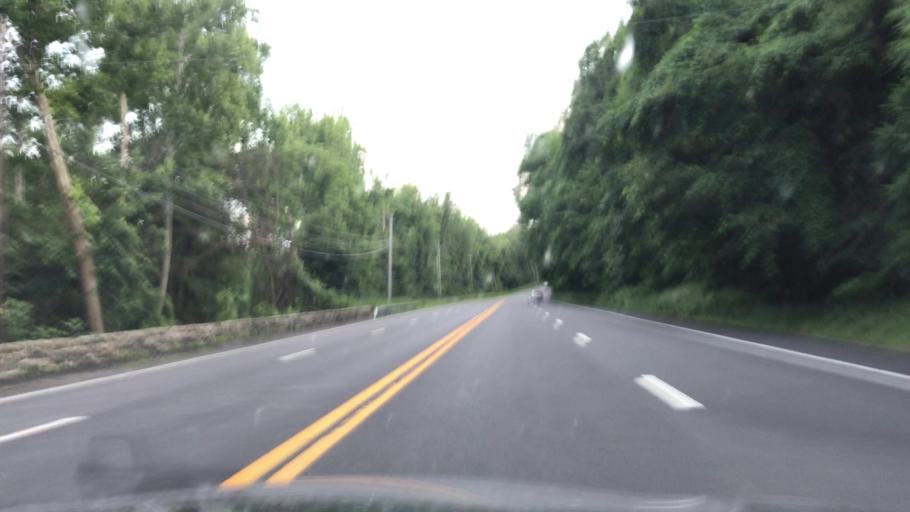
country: US
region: New York
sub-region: Orange County
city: Harriman
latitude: 41.2725
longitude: -74.1539
